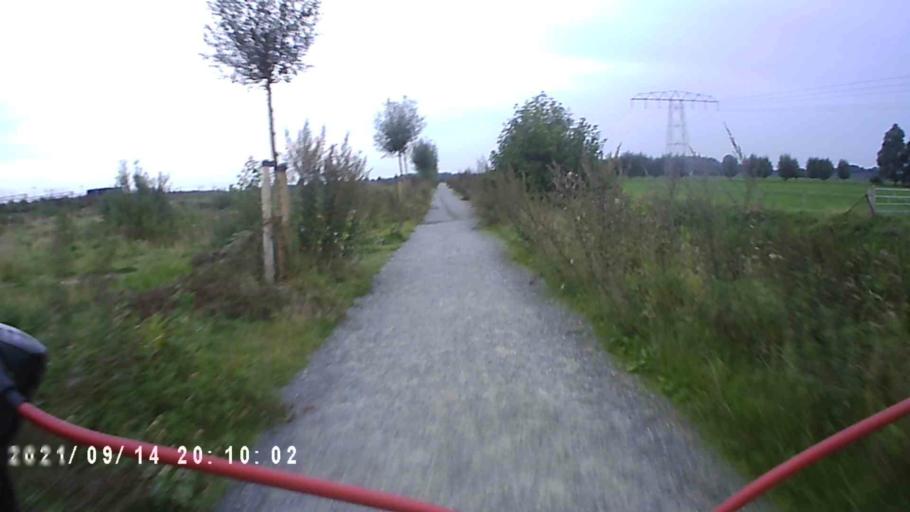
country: NL
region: Groningen
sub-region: Gemeente Haren
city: Haren
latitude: 53.1925
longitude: 6.6115
